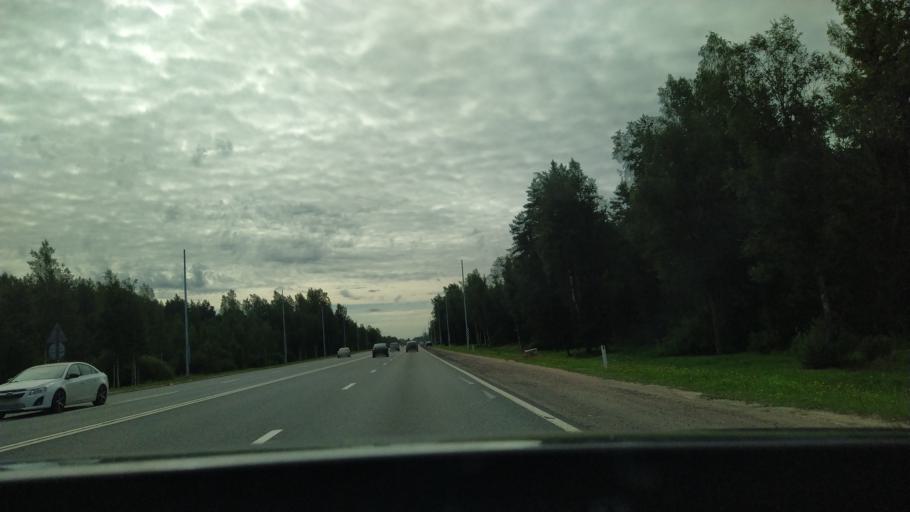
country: RU
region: Leningrad
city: Ul'yanovka
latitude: 59.5780
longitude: 30.8096
